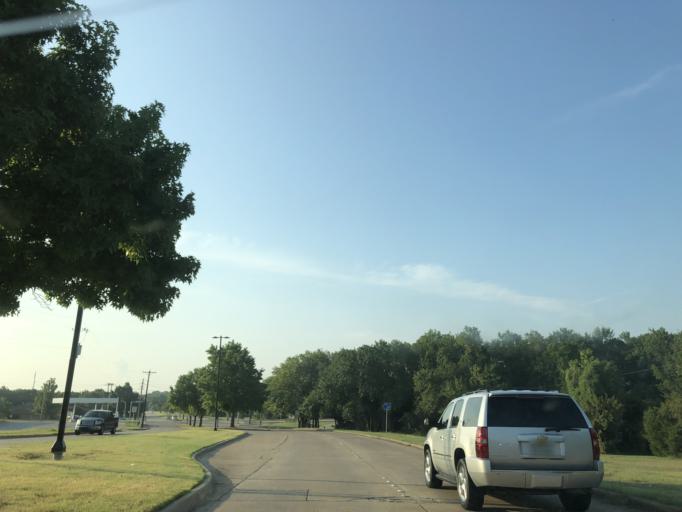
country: US
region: Texas
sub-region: Dallas County
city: Garland
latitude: 32.8526
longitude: -96.6115
